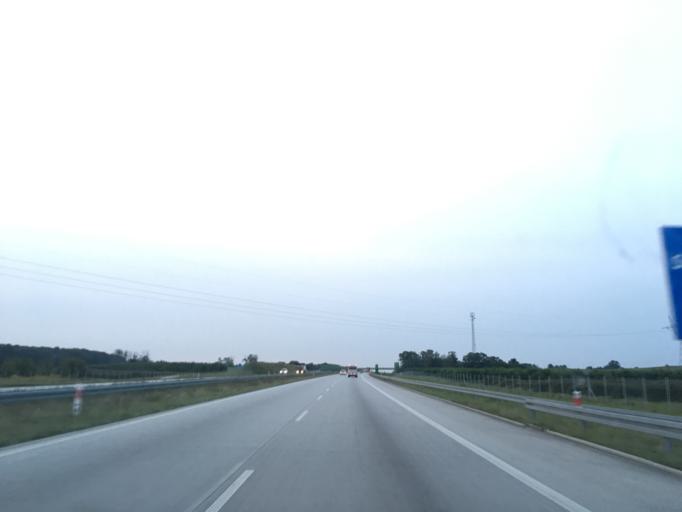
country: PL
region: Lodz Voivodeship
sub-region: Powiat zgierski
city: Strykow
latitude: 51.8630
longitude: 19.6573
